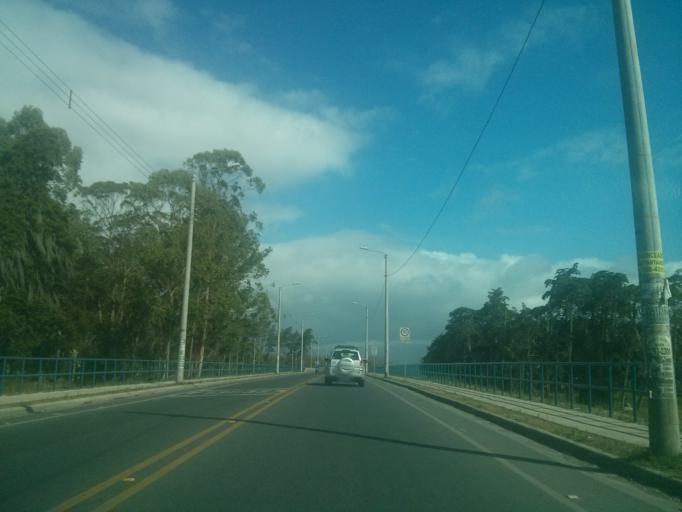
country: CR
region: Cartago
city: Cartago
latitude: 9.8734
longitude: -83.9325
